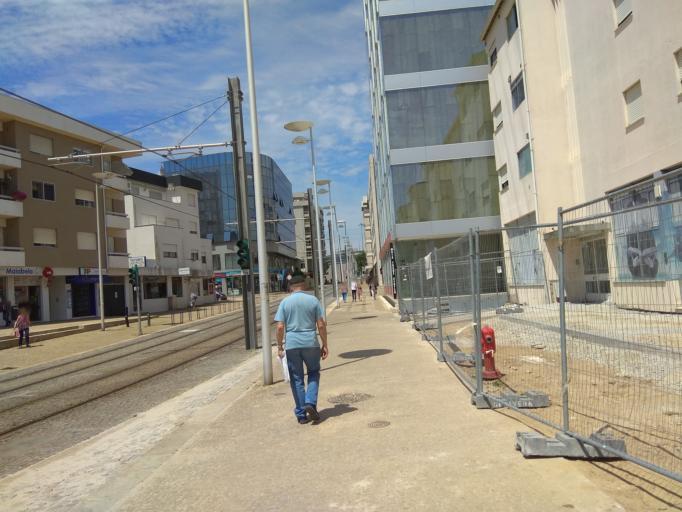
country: PT
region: Porto
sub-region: Maia
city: Maia
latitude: 41.2308
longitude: -8.6226
